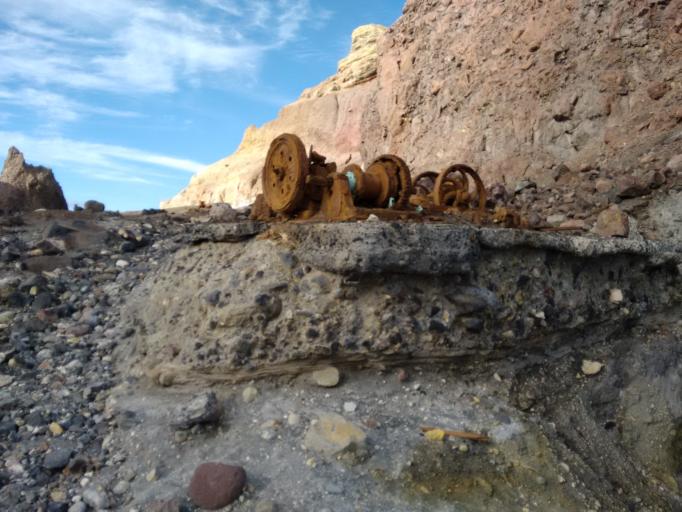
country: NZ
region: Bay of Plenty
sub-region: Whakatane District
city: Whakatane
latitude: -37.5264
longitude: 177.1924
